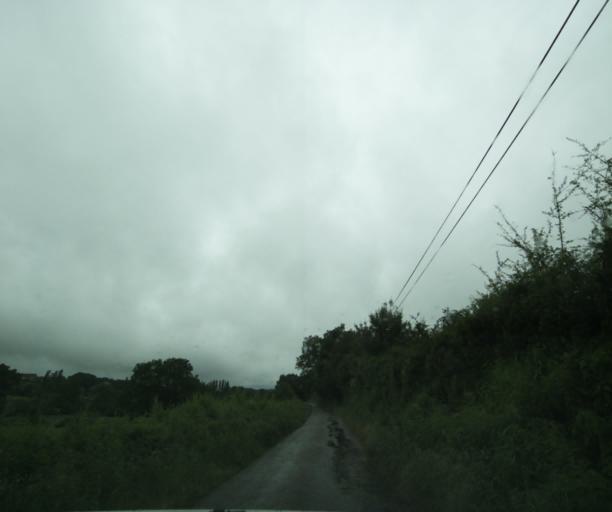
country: FR
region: Bourgogne
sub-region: Departement de Saone-et-Loire
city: Charolles
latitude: 46.4108
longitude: 4.3179
